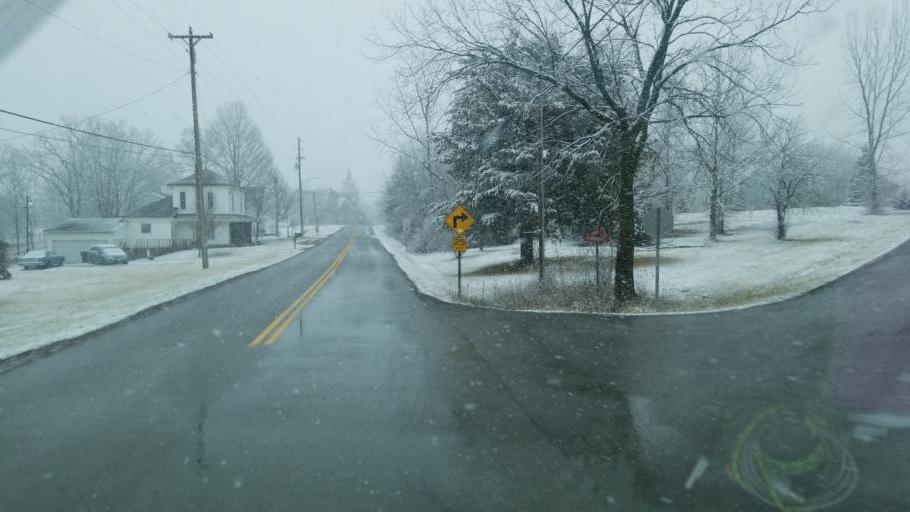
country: US
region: Ohio
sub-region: Champaign County
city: North Lewisburg
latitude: 40.3335
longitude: -83.5863
